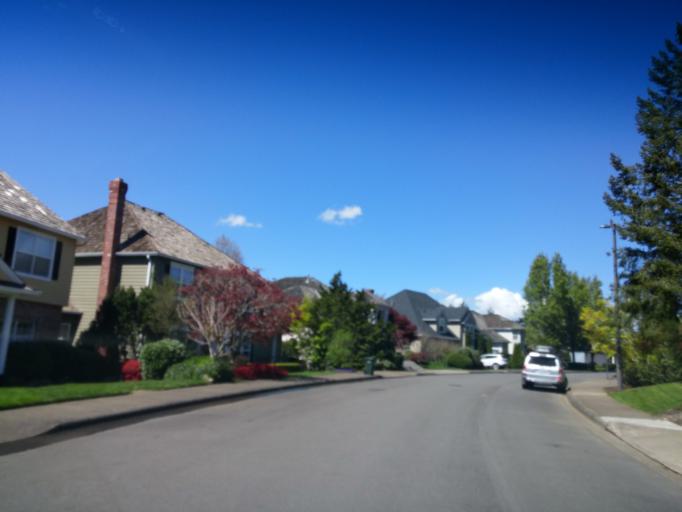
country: US
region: Oregon
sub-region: Washington County
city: West Haven
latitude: 45.5215
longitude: -122.7710
